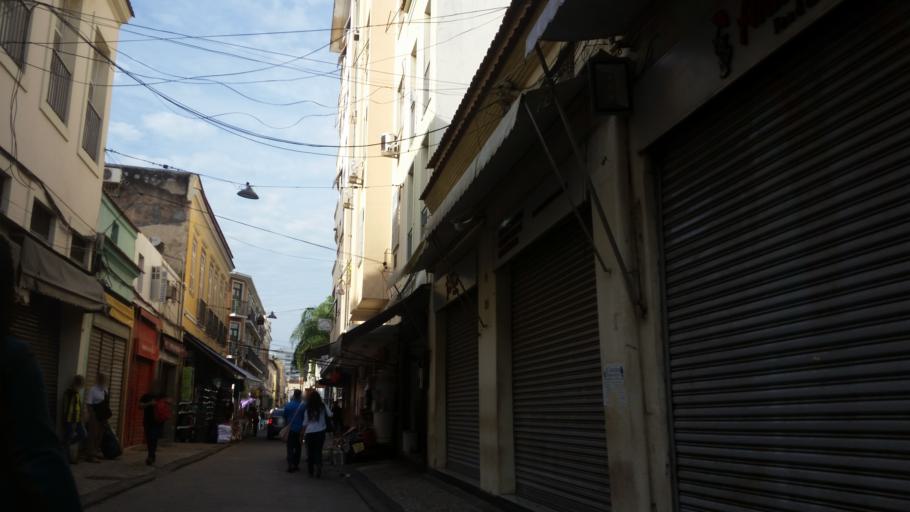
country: BR
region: Rio de Janeiro
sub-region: Rio De Janeiro
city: Rio de Janeiro
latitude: -22.9048
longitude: -43.1851
